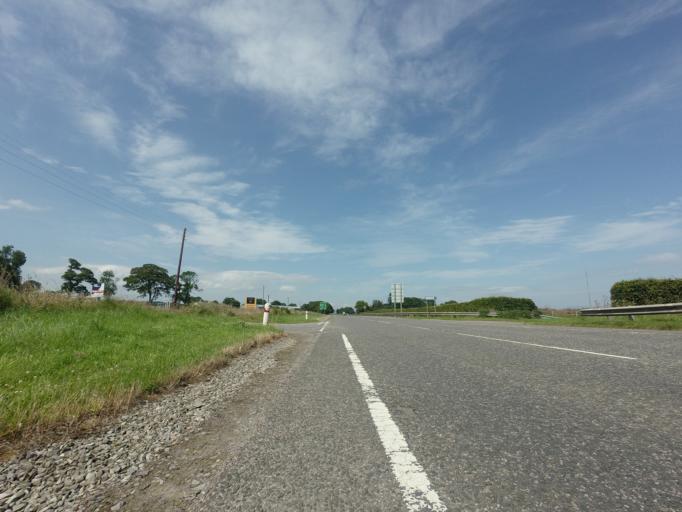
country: GB
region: Scotland
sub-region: Highland
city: Tain
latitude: 57.8209
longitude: -4.0746
